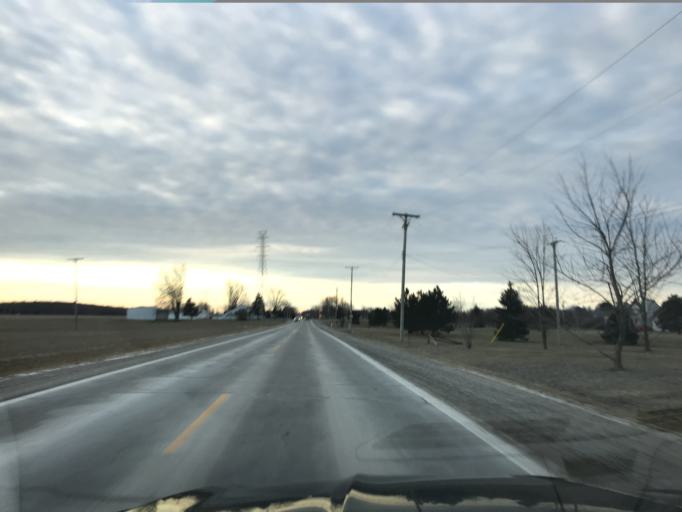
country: US
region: Michigan
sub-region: Macomb County
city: Armada
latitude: 42.8834
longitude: -82.8814
